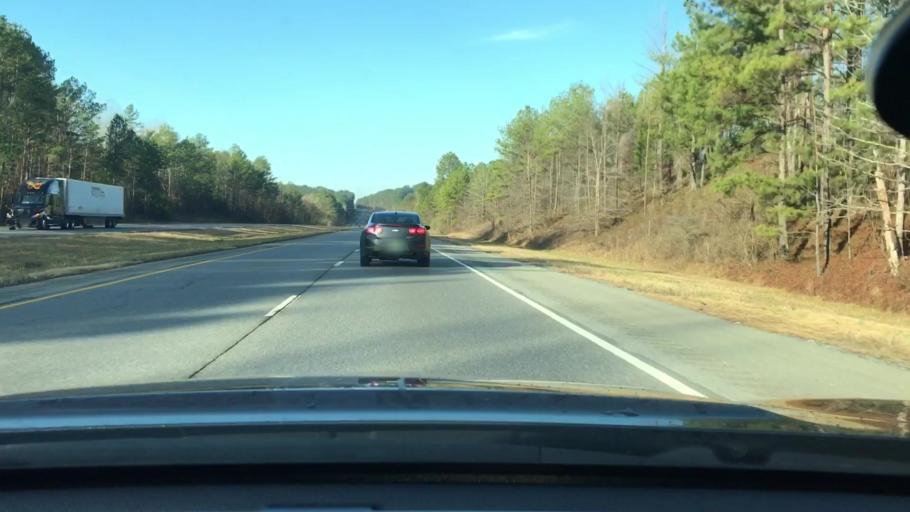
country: US
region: Alabama
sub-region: Shelby County
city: Westover
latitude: 33.3575
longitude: -86.4948
